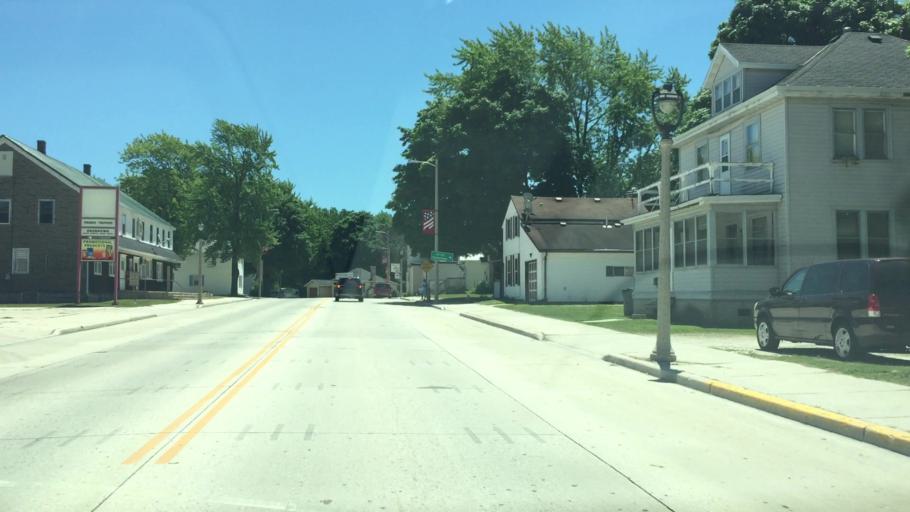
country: US
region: Wisconsin
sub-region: Calumet County
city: New Holstein
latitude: 43.9507
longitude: -88.0995
